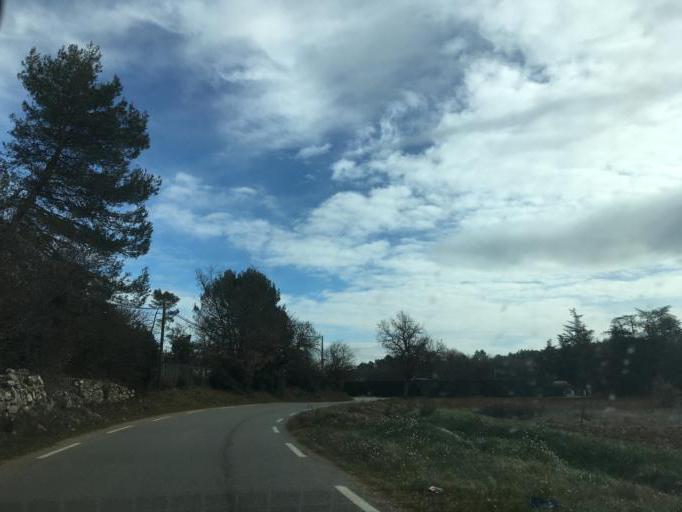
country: FR
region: Provence-Alpes-Cote d'Azur
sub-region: Departement du Var
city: Saint-Maximin-la-Sainte-Baume
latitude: 43.4533
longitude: 5.8880
